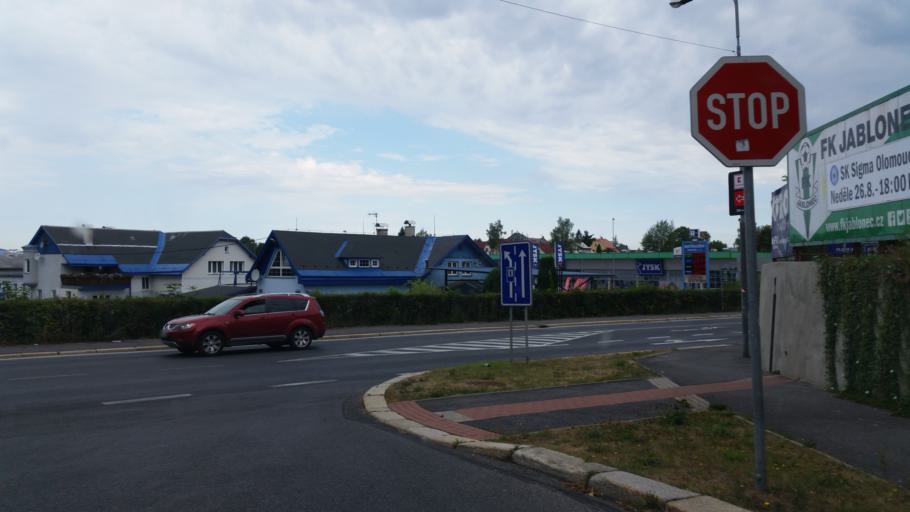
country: CZ
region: Liberecky
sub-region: Okres Jablonec nad Nisou
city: Jablonec nad Nisou
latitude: 50.7150
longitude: 15.1613
